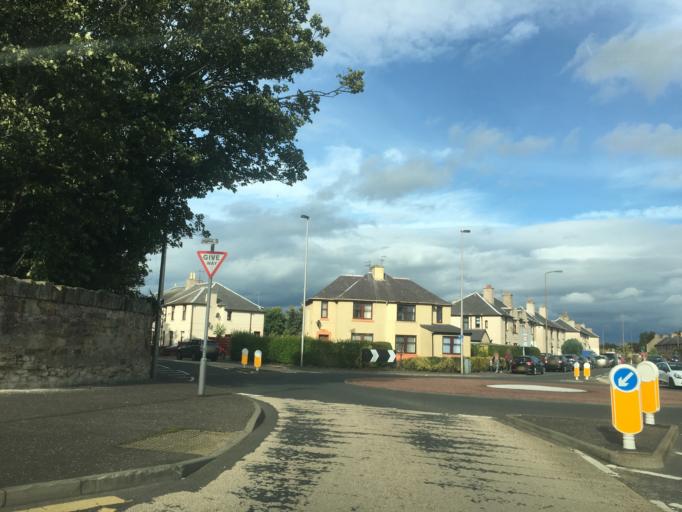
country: GB
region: Scotland
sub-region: East Lothian
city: Musselburgh
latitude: 55.9191
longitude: -3.0423
